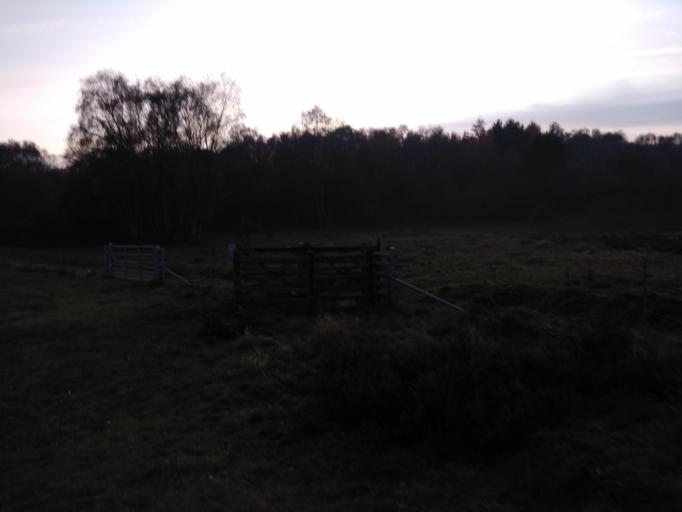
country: GB
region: England
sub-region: Nottinghamshire
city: Worksop
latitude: 53.2678
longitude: -1.0748
